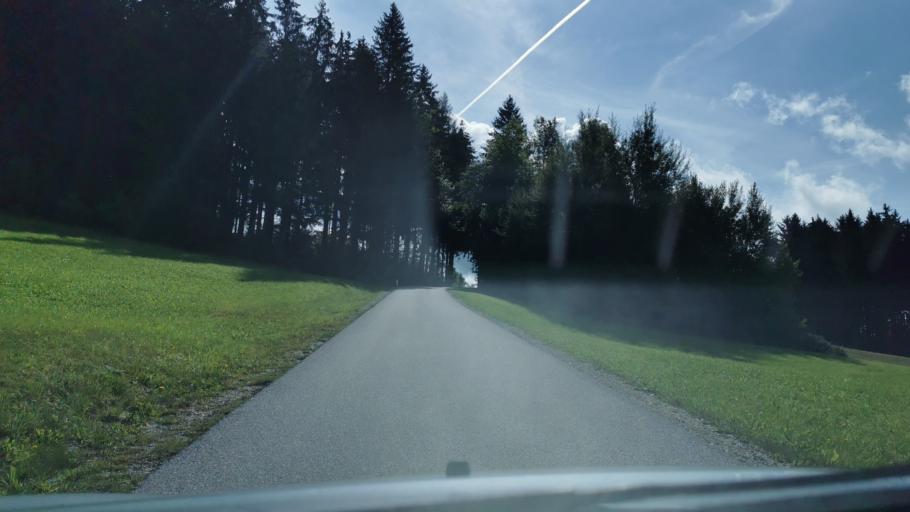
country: AT
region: Styria
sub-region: Politischer Bezirk Weiz
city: Baierdorf-Umgebung
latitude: 47.3015
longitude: 15.7033
